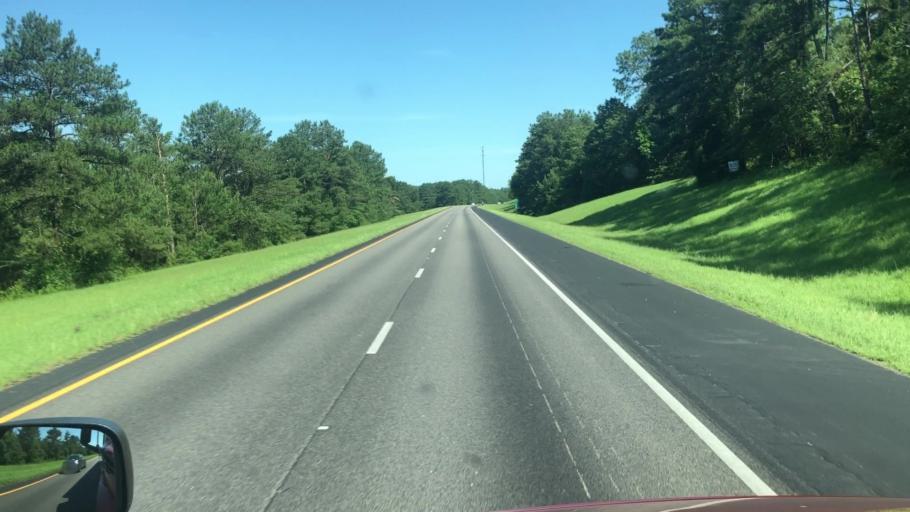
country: US
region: Alabama
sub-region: Autauga County
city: Prattville
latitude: 32.5198
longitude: -86.4353
